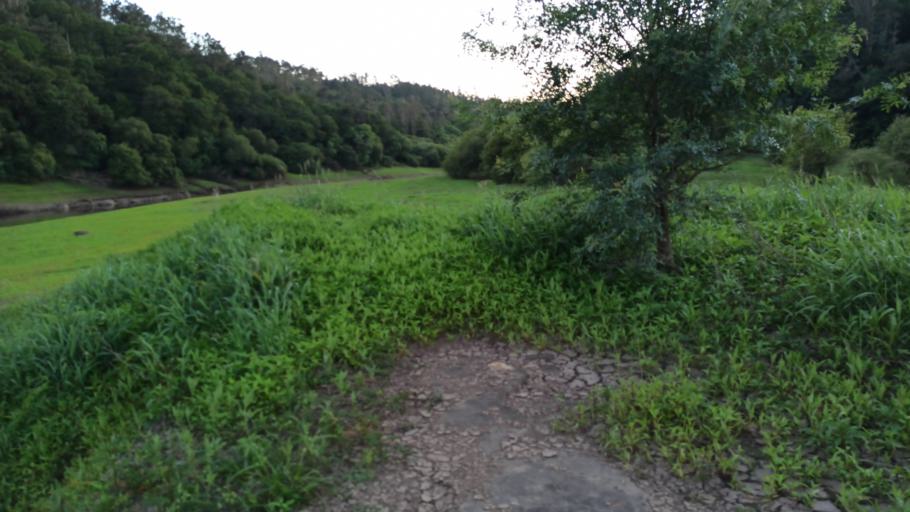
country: ES
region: Galicia
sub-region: Provincia da Coruna
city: Negreira
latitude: 42.8984
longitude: -8.7368
